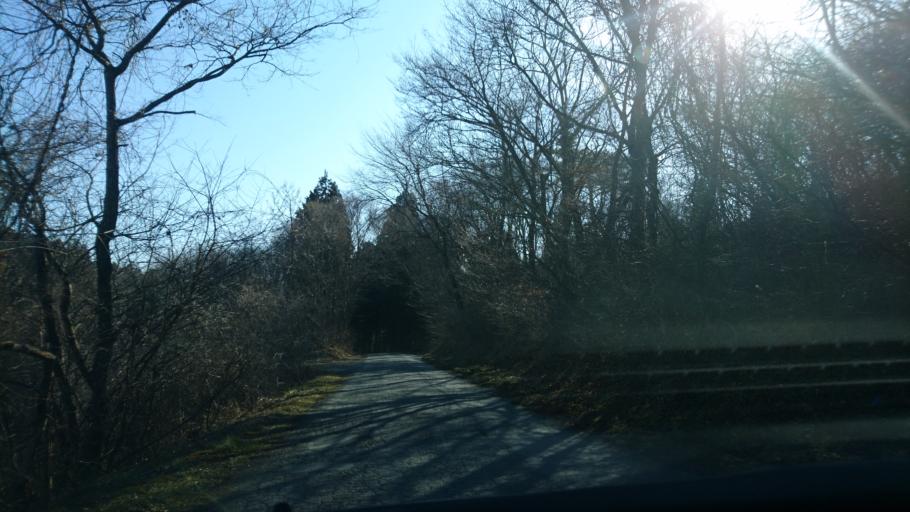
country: JP
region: Iwate
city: Ichinoseki
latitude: 38.8101
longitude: 141.2665
